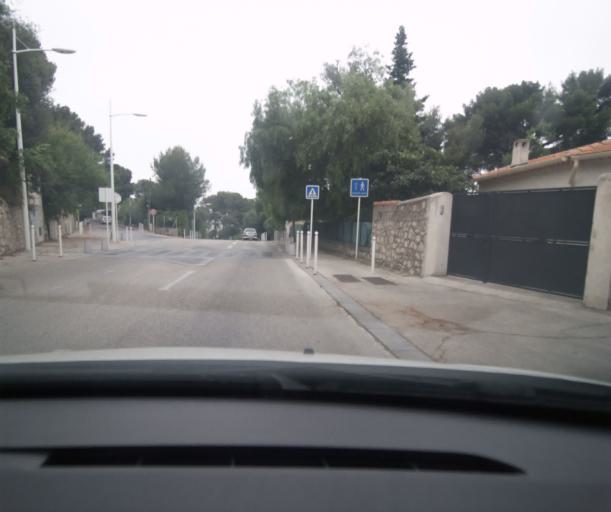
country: FR
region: Provence-Alpes-Cote d'Azur
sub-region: Departement du Var
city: La Valette-du-Var
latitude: 43.1352
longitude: 5.9699
